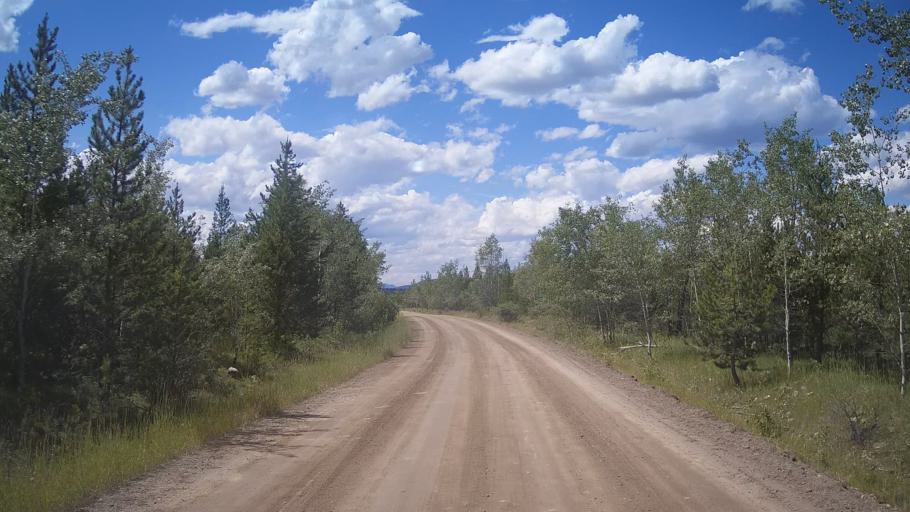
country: CA
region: British Columbia
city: Lillooet
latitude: 51.3410
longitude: -121.9238
